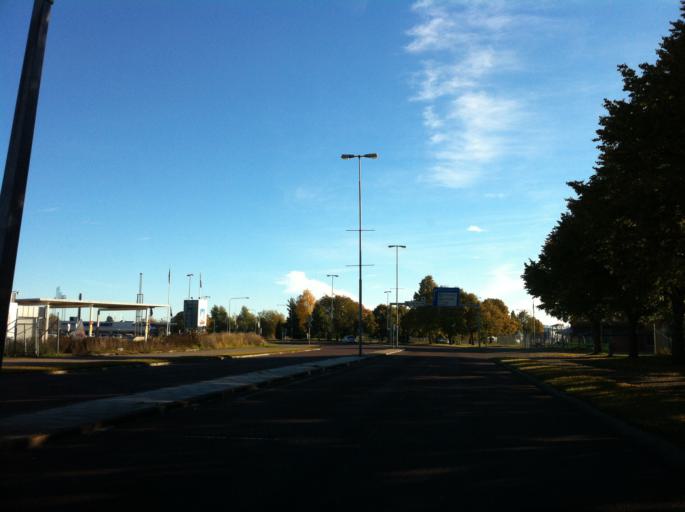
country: SE
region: Gaevleborg
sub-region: Gavle Kommun
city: Gavle
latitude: 60.6591
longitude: 17.1554
